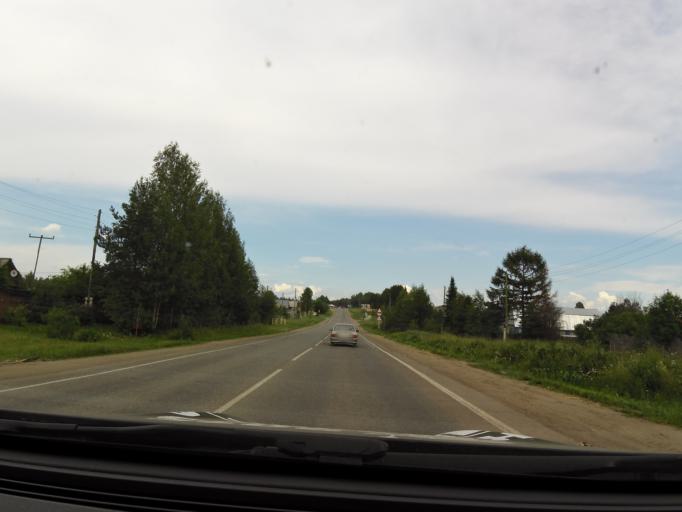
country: RU
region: Kirov
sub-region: Kirovo-Chepetskiy Rayon
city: Kirov
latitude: 58.6315
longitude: 49.8182
